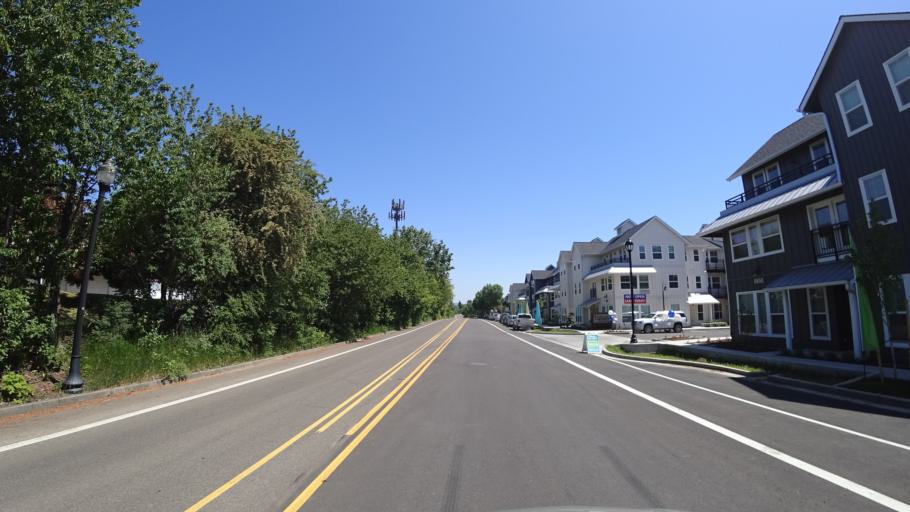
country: US
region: Oregon
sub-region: Washington County
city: Rockcreek
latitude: 45.5311
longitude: -122.9102
